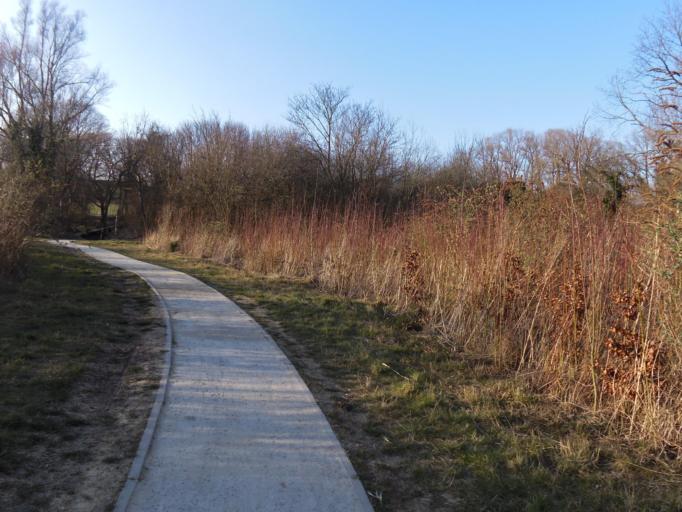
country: BE
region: Flanders
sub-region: Provincie Vlaams-Brabant
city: Wezembeek-Oppem
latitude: 50.8619
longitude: 4.4937
